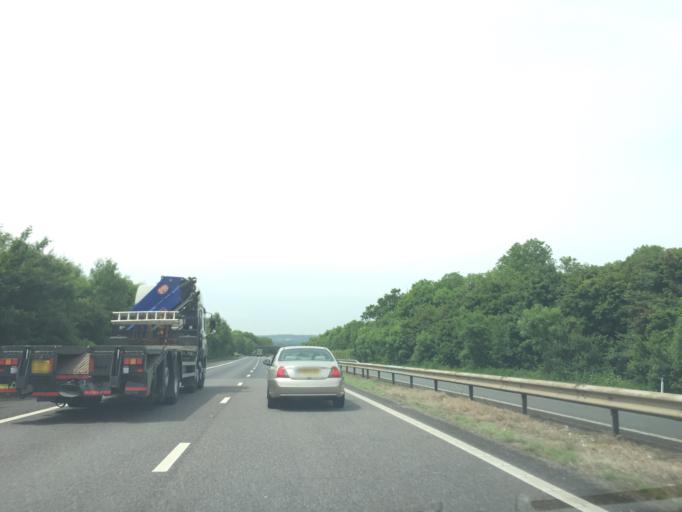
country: GB
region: England
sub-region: Kent
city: Kemsing
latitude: 51.3010
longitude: 0.2369
